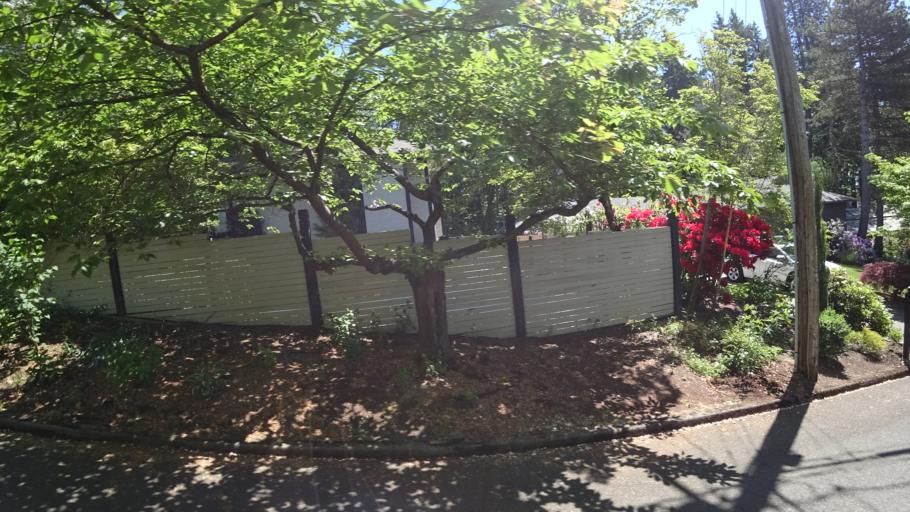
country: US
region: Oregon
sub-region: Washington County
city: Raleigh Hills
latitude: 45.4932
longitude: -122.7185
